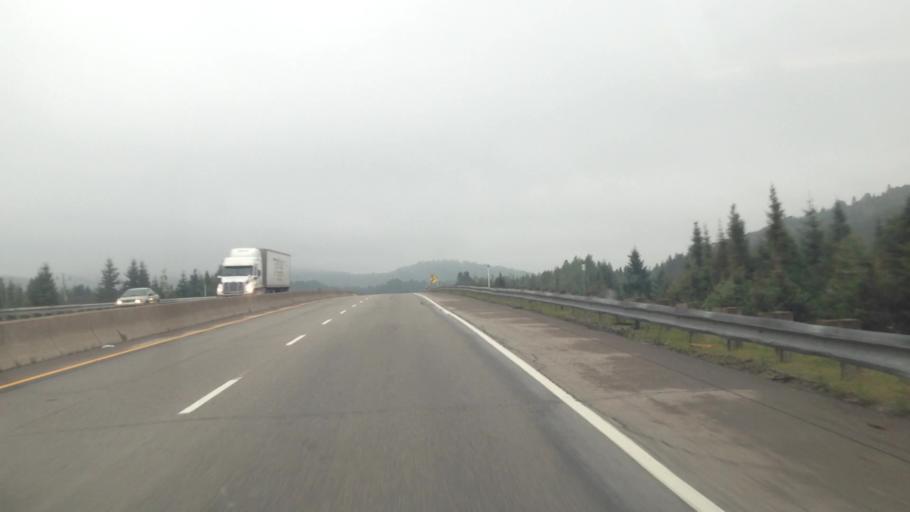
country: CA
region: Quebec
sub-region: Laurentides
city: Sainte-Agathe-des-Monts
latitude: 46.0982
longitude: -74.3648
